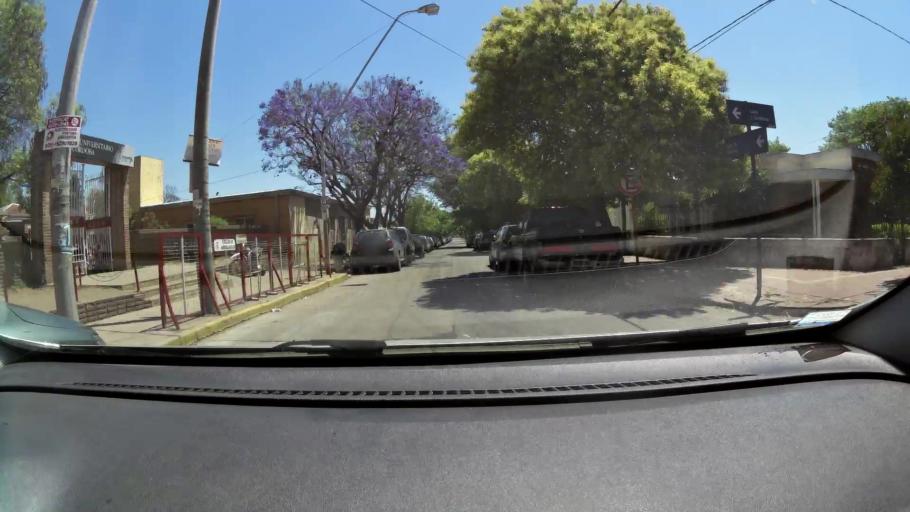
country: AR
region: Cordoba
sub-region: Departamento de Capital
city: Cordoba
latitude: -31.4136
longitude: -64.2150
